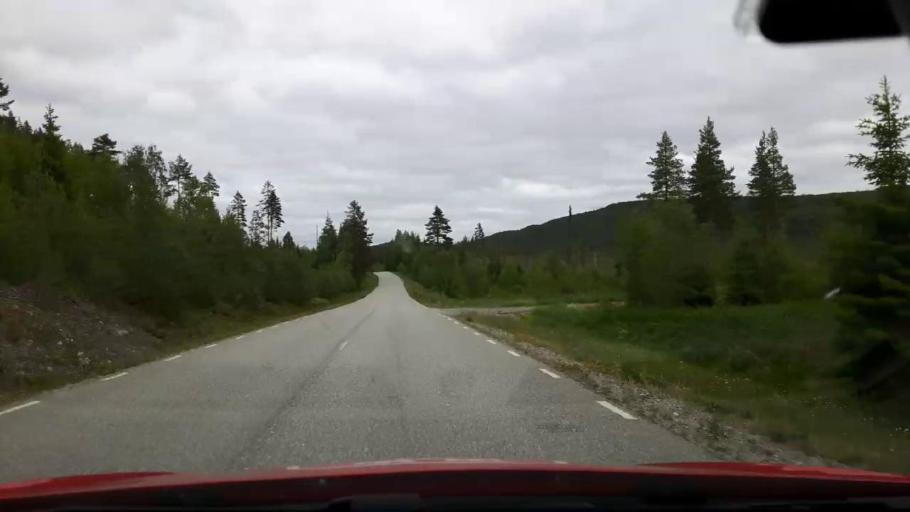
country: SE
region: Jaemtland
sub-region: Ragunda Kommun
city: Hammarstrand
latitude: 63.2106
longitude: 15.9974
